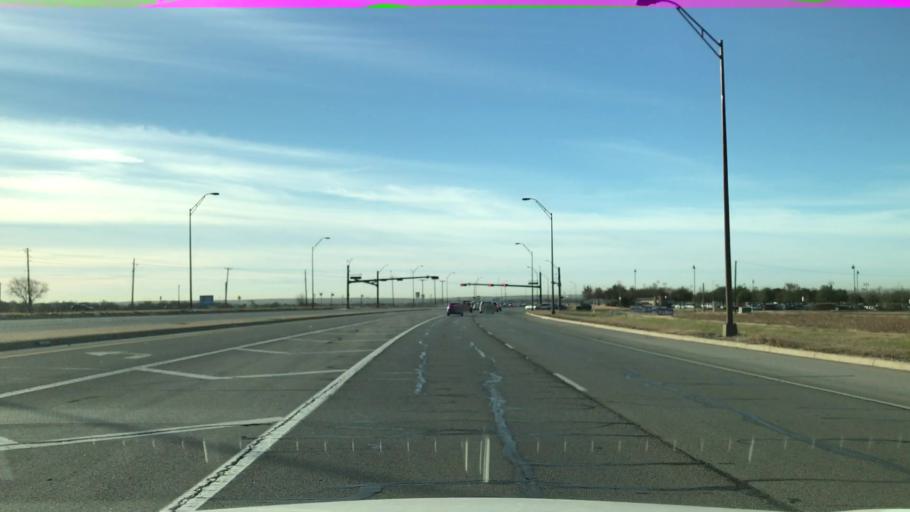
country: US
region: Texas
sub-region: Williamson County
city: Round Rock
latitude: 30.5604
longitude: -97.6460
